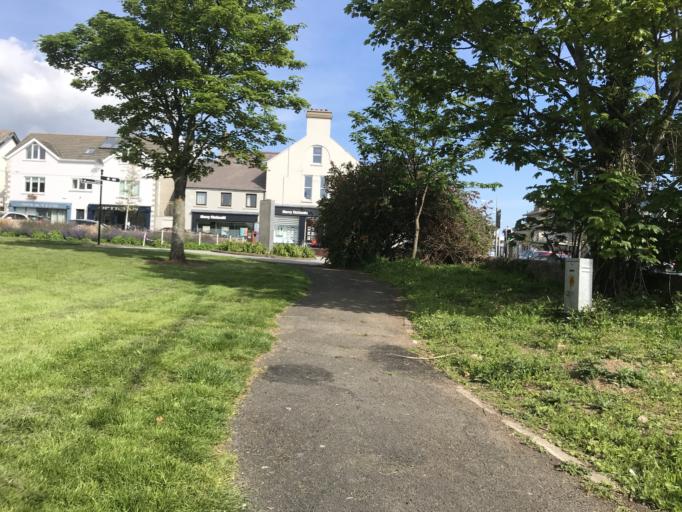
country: IE
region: Leinster
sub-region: Wicklow
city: Greystones
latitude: 53.1433
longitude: -6.0609
